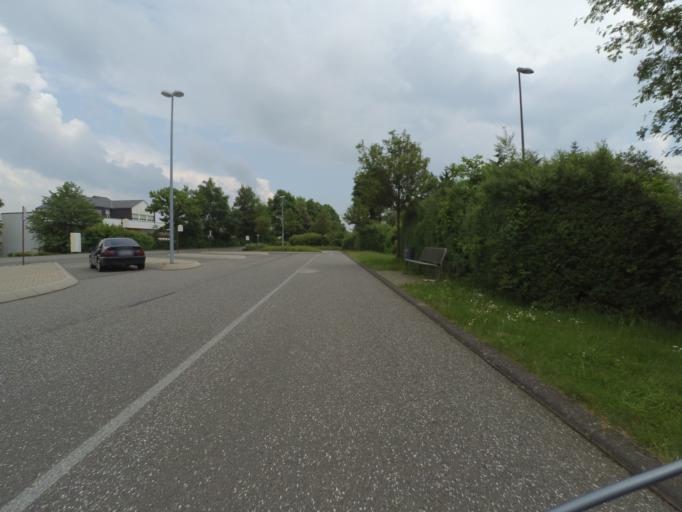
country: DE
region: Rheinland-Pfalz
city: Kastellaun
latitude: 50.0670
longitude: 7.4482
